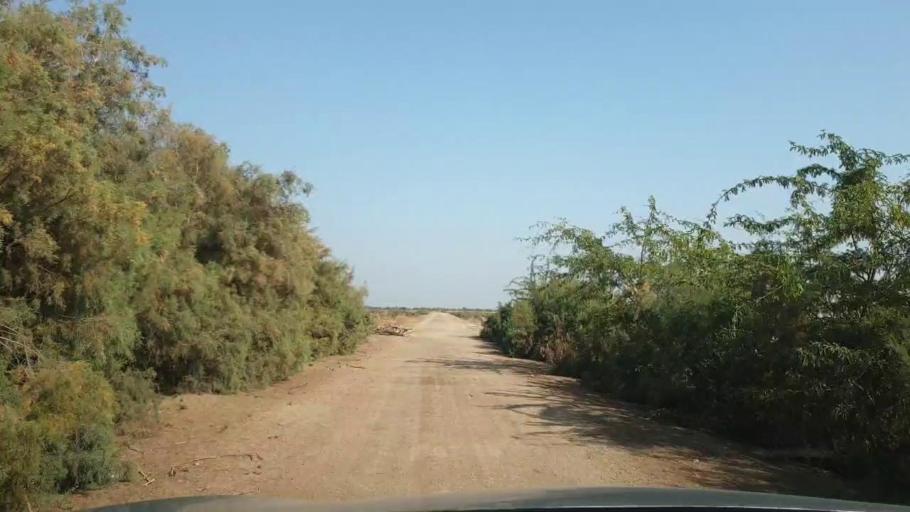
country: PK
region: Sindh
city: Berani
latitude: 25.6223
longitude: 68.8358
